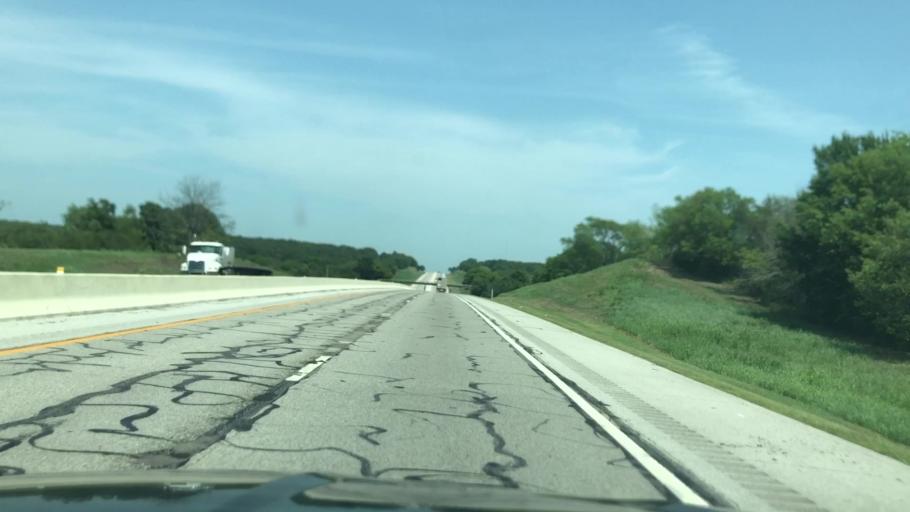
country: US
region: Oklahoma
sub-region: Rogers County
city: Chelsea
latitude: 36.4604
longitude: -95.3497
